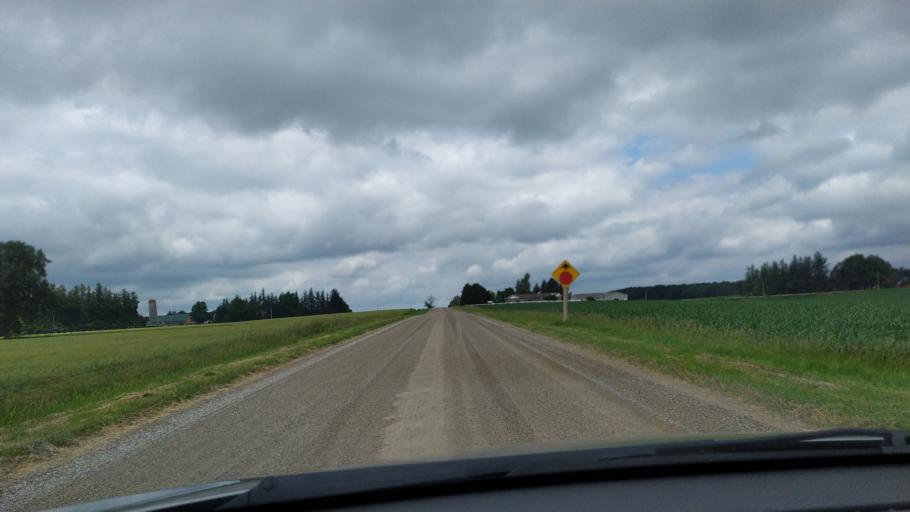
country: CA
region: Ontario
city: Stratford
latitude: 43.4220
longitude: -80.8883
